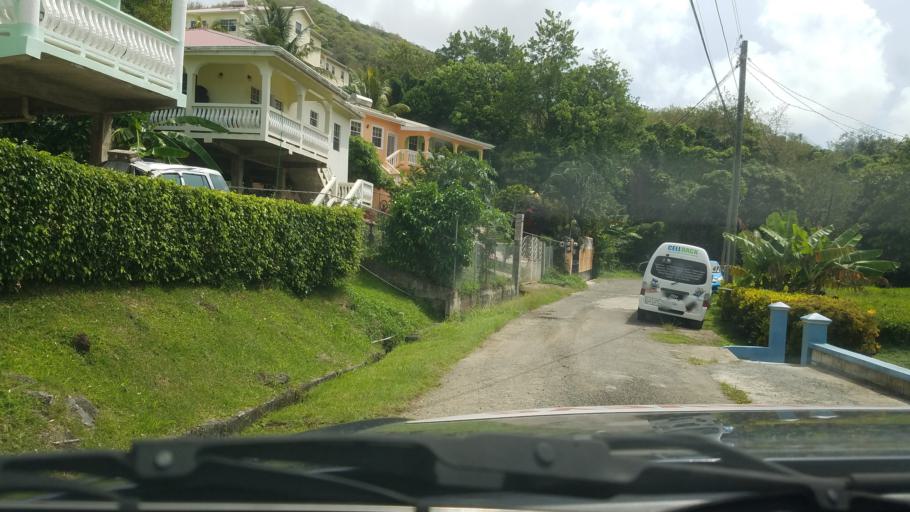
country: LC
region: Gros-Islet
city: Gros Islet
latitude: 14.0461
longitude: -60.9555
